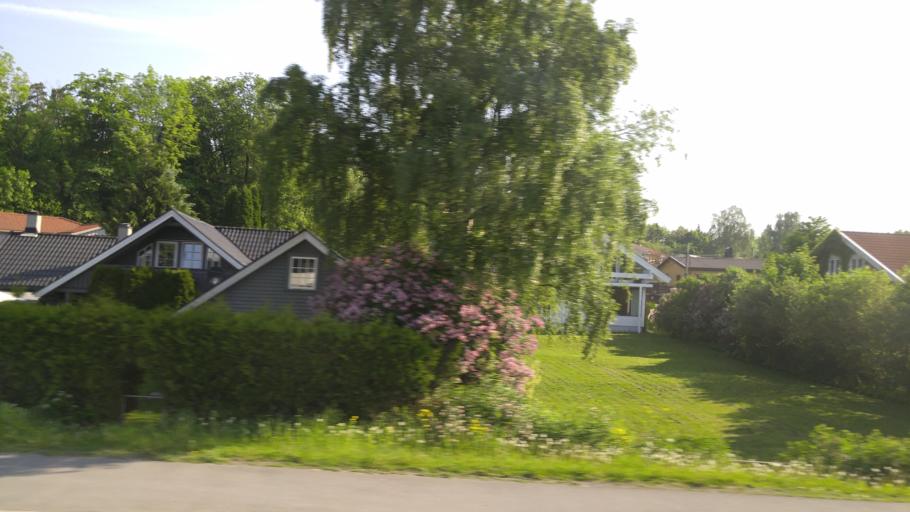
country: NO
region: Akershus
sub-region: Baerum
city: Sandvika
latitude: 59.8938
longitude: 10.5513
